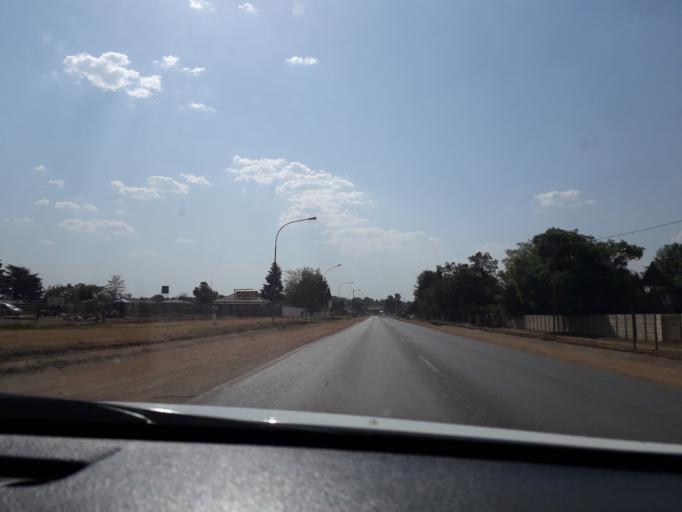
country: ZA
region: Gauteng
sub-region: Ekurhuleni Metropolitan Municipality
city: Tembisa
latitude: -26.0836
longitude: 28.2918
